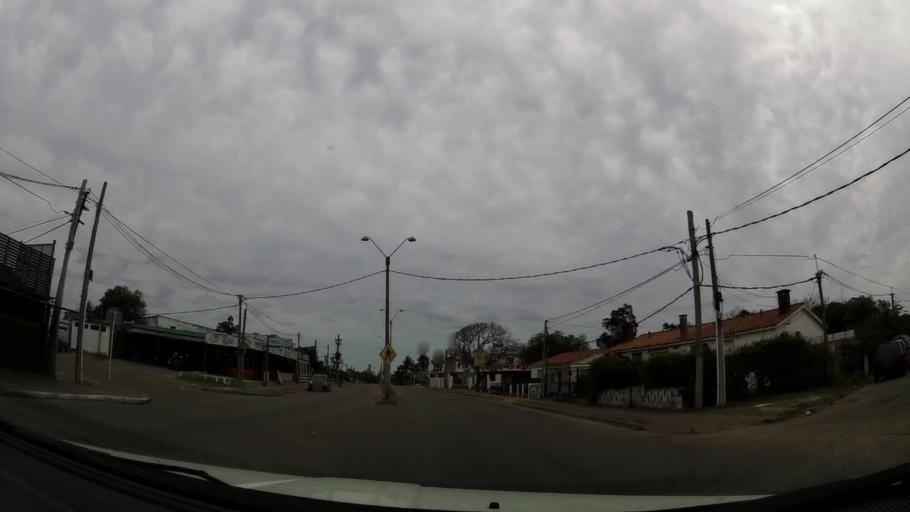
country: UY
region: Maldonado
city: Maldonado
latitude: -34.9139
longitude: -54.9677
